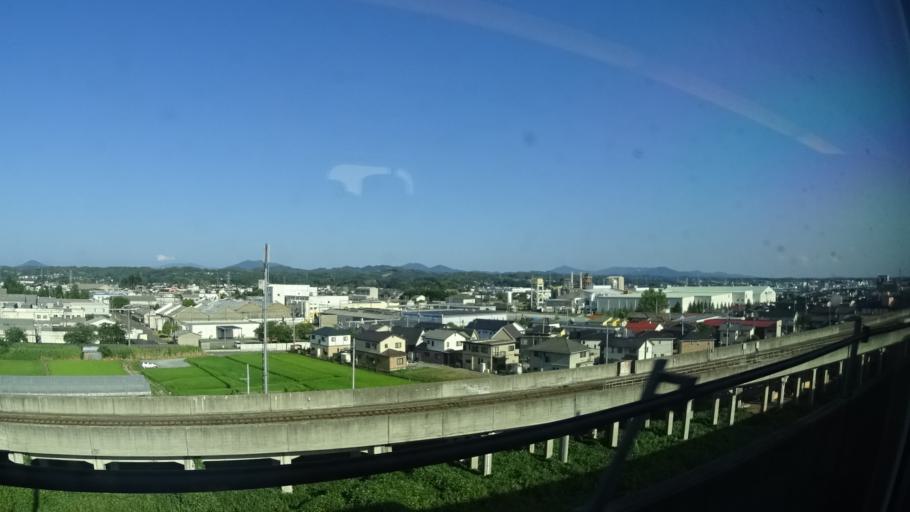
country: JP
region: Fukushima
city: Koriyama
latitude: 37.4207
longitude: 140.3956
